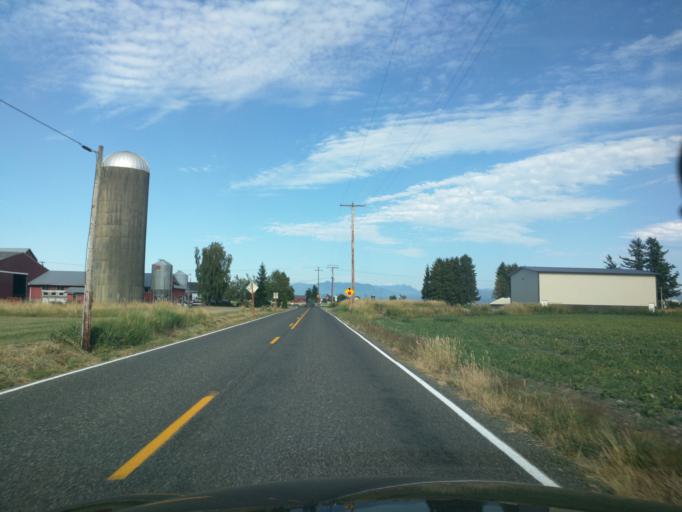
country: US
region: Washington
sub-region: Whatcom County
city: Lynden
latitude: 48.9933
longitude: -122.4876
